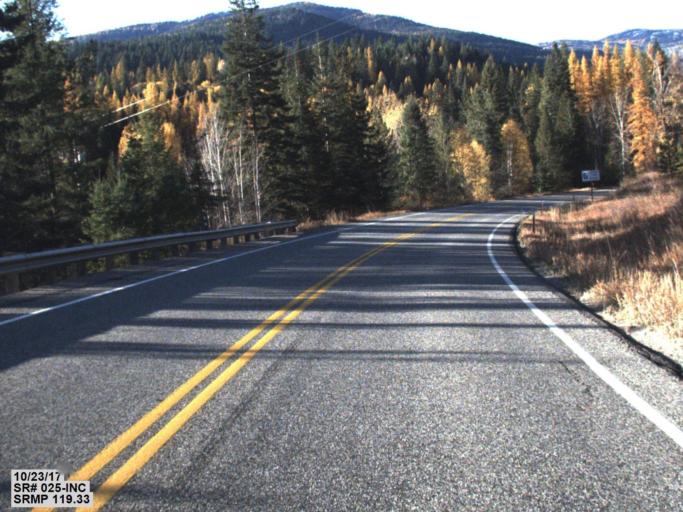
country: CA
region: British Columbia
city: Rossland
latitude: 48.9751
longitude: -117.8194
